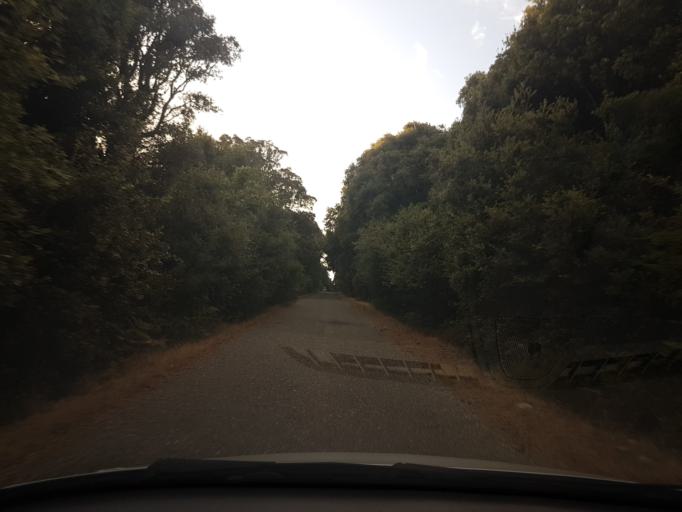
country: IT
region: Sardinia
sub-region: Provincia di Oristano
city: Seneghe
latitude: 40.1078
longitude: 8.5883
